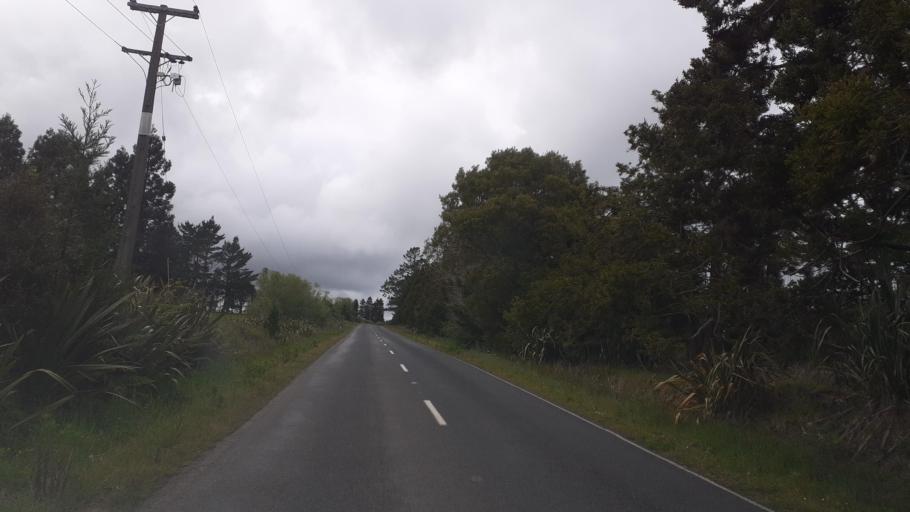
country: NZ
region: Northland
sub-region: Far North District
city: Waimate North
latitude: -35.2572
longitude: 173.8015
